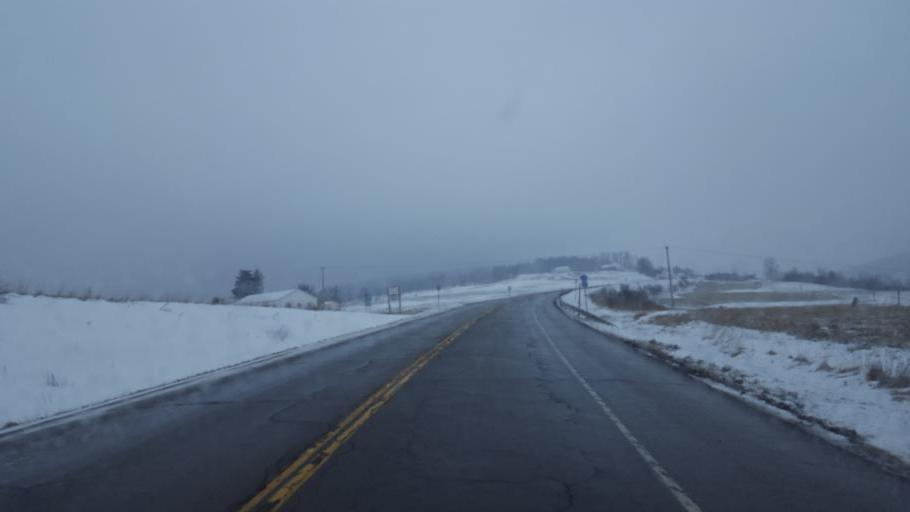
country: US
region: New York
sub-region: Steuben County
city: Canisteo
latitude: 42.1318
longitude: -77.5154
